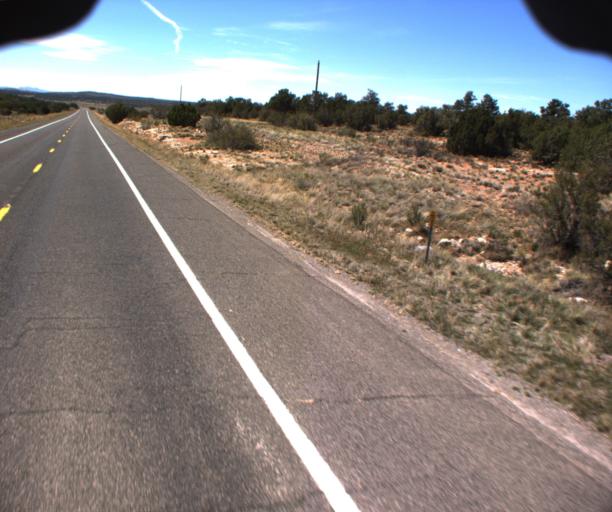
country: US
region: Arizona
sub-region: Mohave County
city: Peach Springs
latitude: 35.5487
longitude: -113.2998
